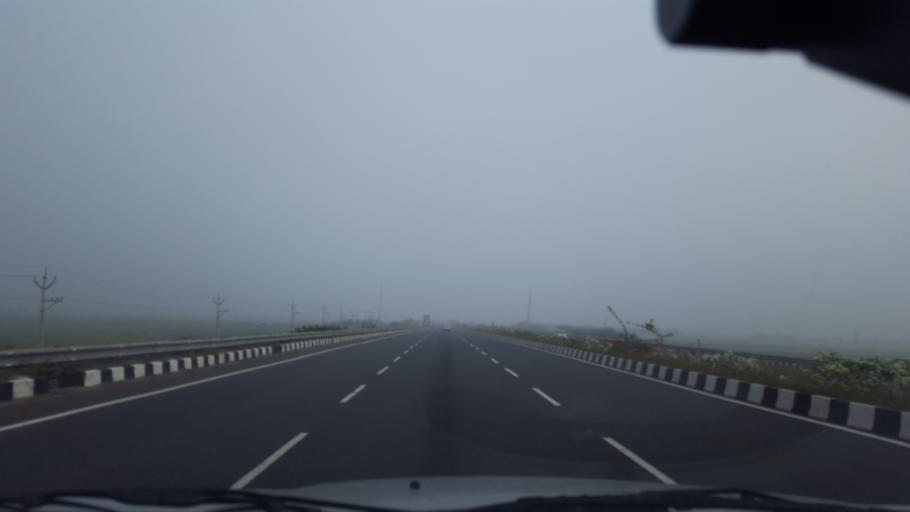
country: IN
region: Andhra Pradesh
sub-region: Prakasam
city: Ongole
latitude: 15.4772
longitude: 80.0590
